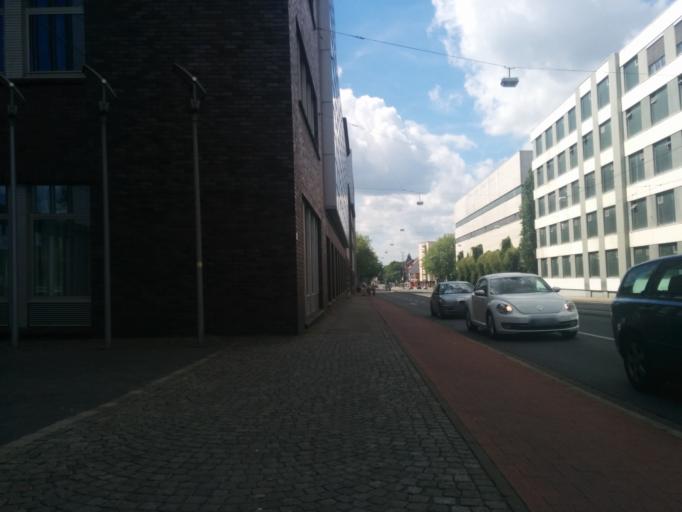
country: DE
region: Bremen
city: Bremen
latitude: 53.0763
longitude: 8.7973
